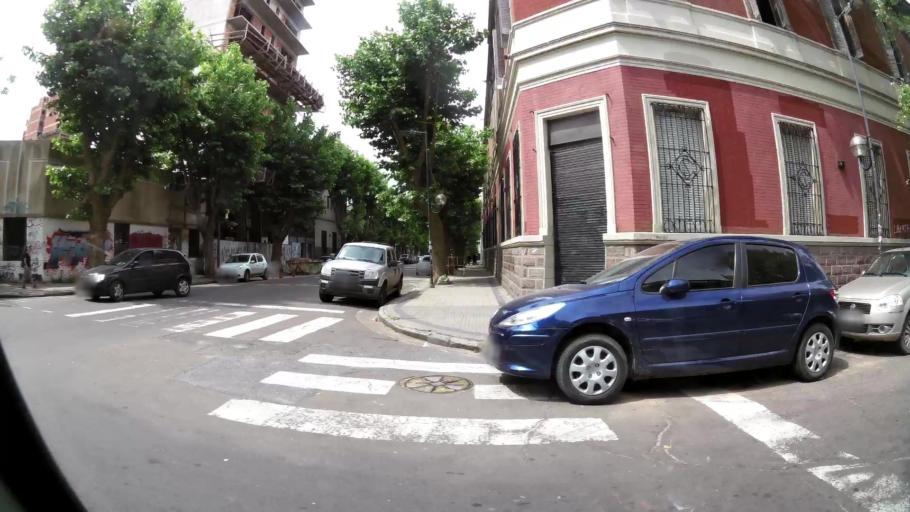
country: AR
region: Buenos Aires
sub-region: Partido de La Plata
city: La Plata
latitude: -34.9205
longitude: -57.9468
